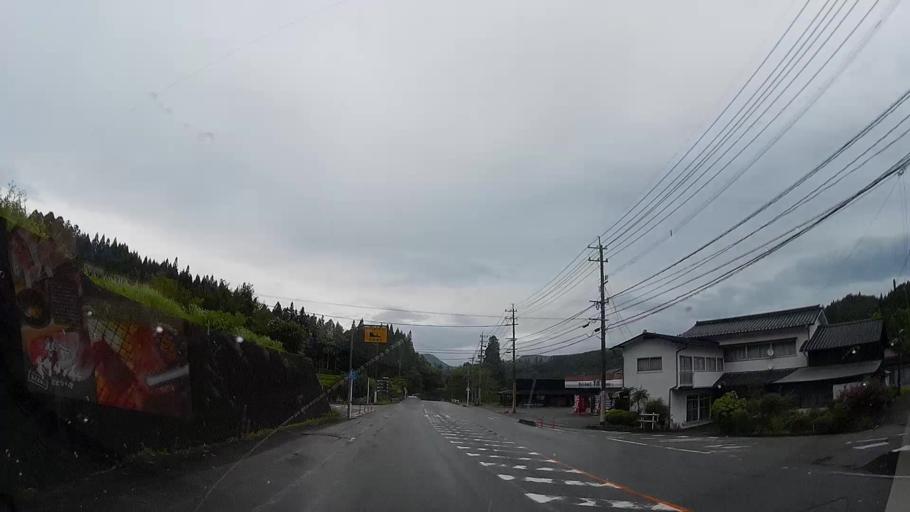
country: JP
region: Oita
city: Tsukawaki
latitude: 33.1483
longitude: 131.0543
